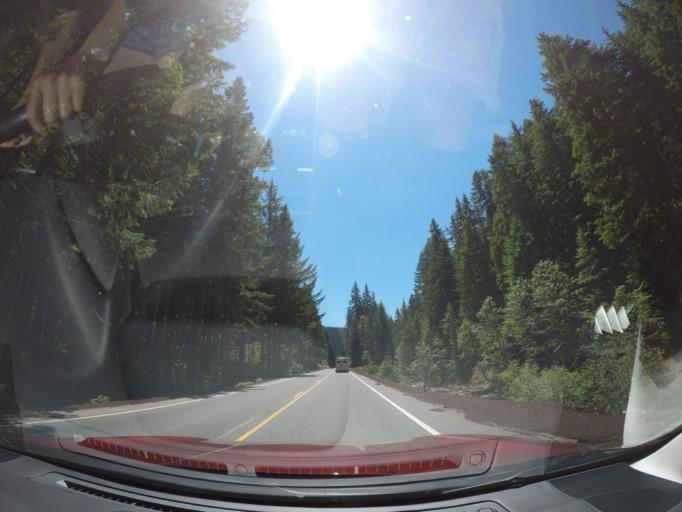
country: US
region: Oregon
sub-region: Linn County
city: Mill City
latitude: 44.5598
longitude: -121.9985
